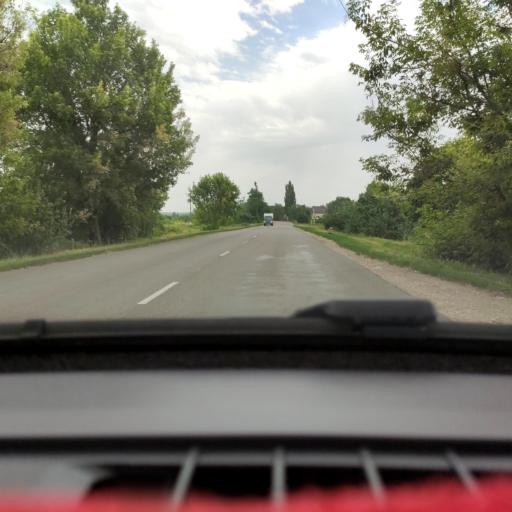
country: RU
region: Voronezj
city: Davydovka
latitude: 51.1934
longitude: 39.4971
